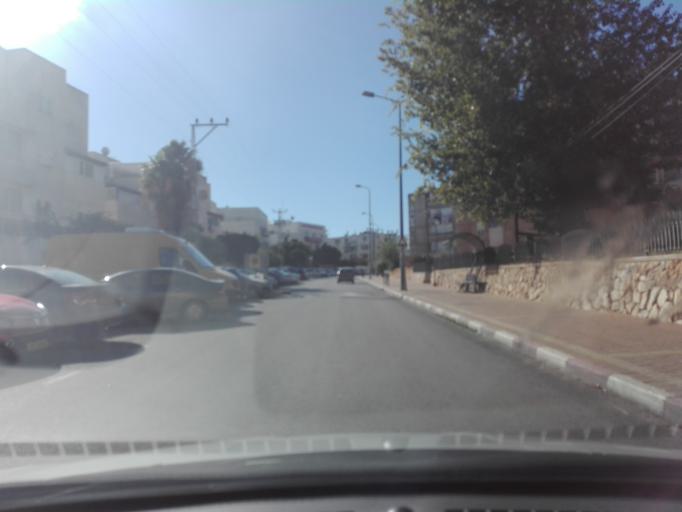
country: IL
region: Central District
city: Netanya
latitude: 32.3009
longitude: 34.8584
